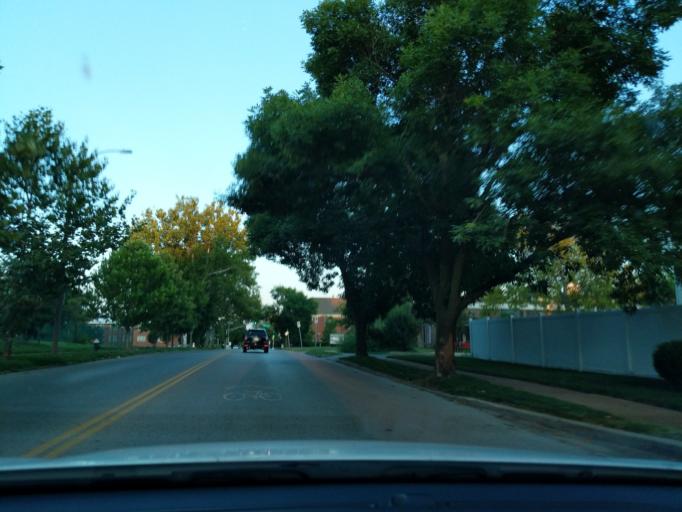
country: US
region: Missouri
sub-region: Saint Louis County
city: Maplewood
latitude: 38.6064
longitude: -90.2830
